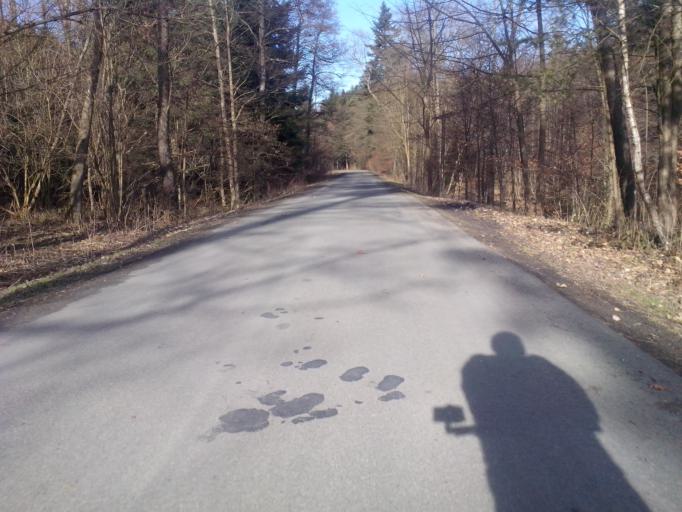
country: PL
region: Subcarpathian Voivodeship
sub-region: Powiat strzyzowski
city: Strzyzow
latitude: 49.8043
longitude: 21.8279
